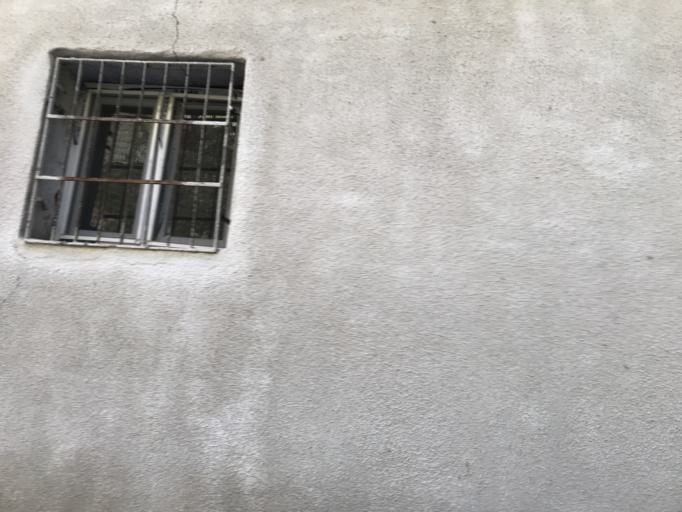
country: TR
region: Hatay
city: Buyukcat
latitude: 36.0781
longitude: 36.0421
